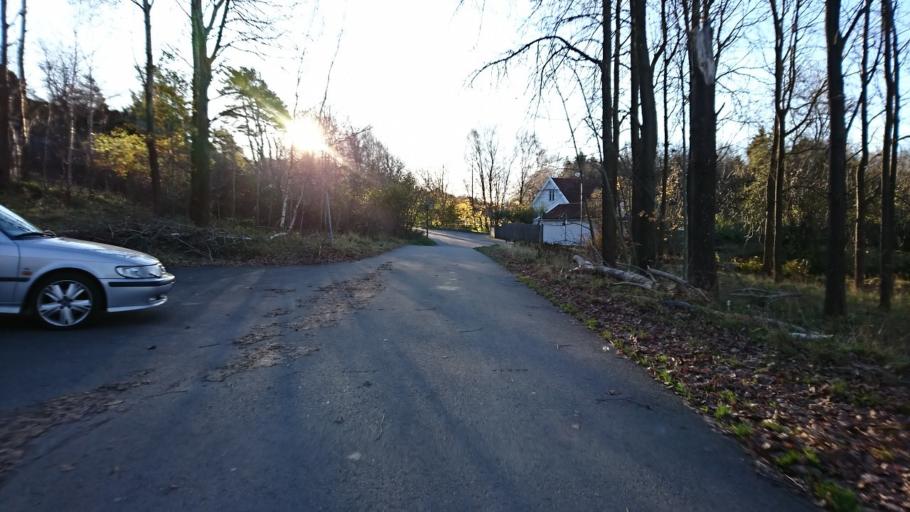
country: SE
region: Vaestra Goetaland
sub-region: Molndal
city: Moelndal
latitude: 57.6829
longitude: 12.0221
